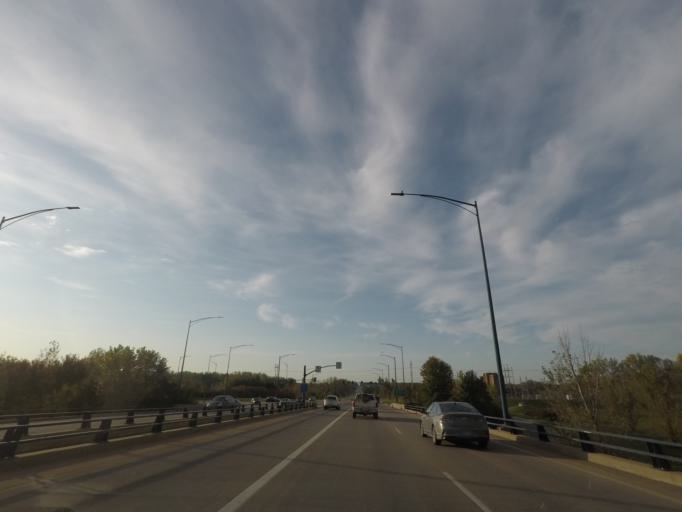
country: US
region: Iowa
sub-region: Polk County
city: Des Moines
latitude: 41.5813
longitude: -93.6449
